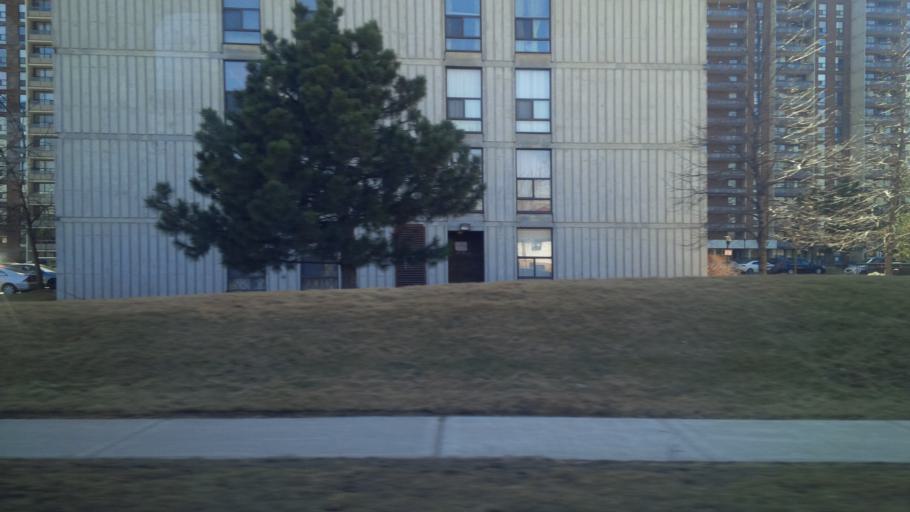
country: CA
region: Ontario
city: Brampton
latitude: 43.7209
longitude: -79.7128
